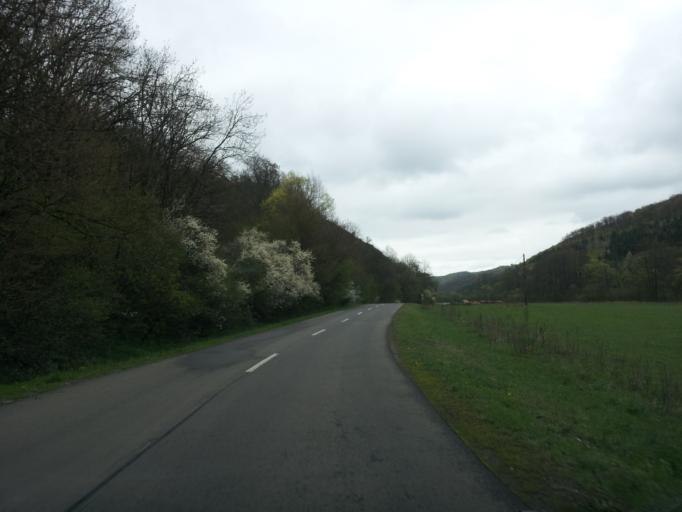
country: HU
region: Borsod-Abauj-Zemplen
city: Rudabanya
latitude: 48.4787
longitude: 20.5762
